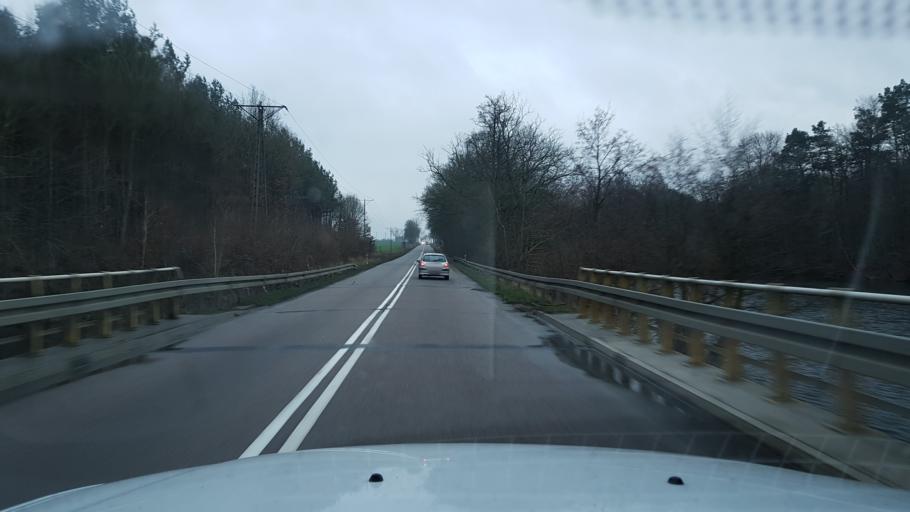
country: PL
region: West Pomeranian Voivodeship
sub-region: Powiat gryficki
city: Gryfice
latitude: 53.8579
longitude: 15.2262
